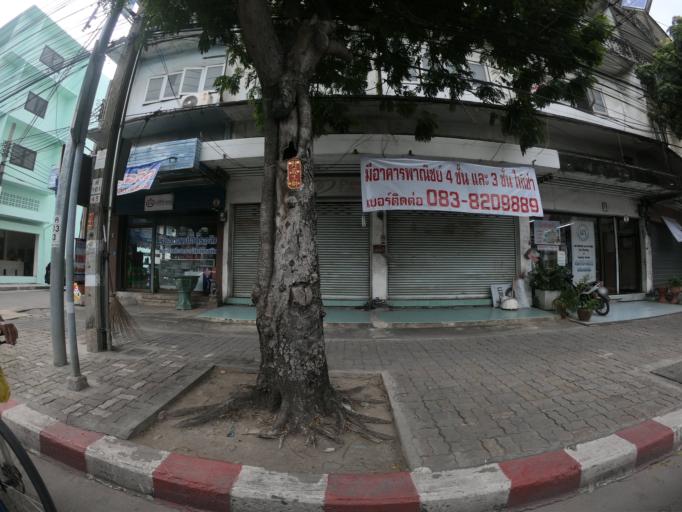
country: TH
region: Bangkok
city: Bang Na
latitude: 13.6767
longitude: 100.6617
